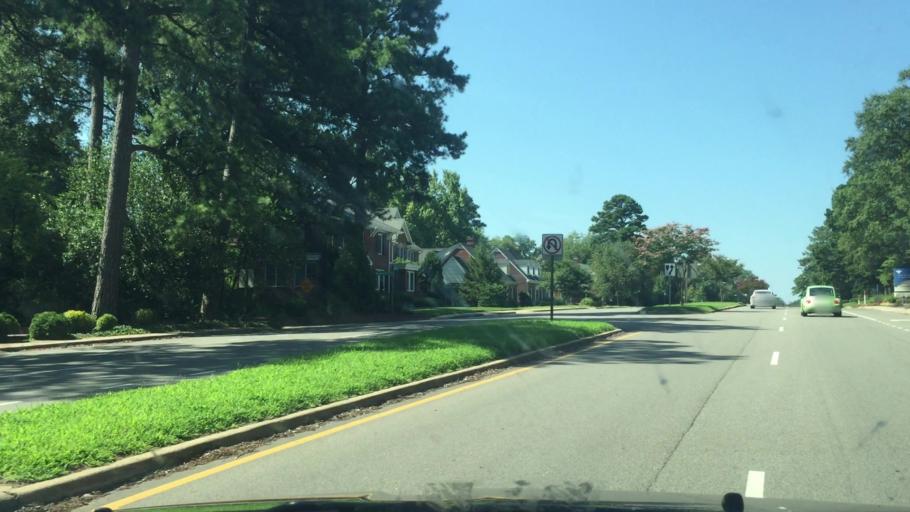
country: US
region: Virginia
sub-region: Henrico County
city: Dumbarton
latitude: 37.5832
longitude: -77.5106
